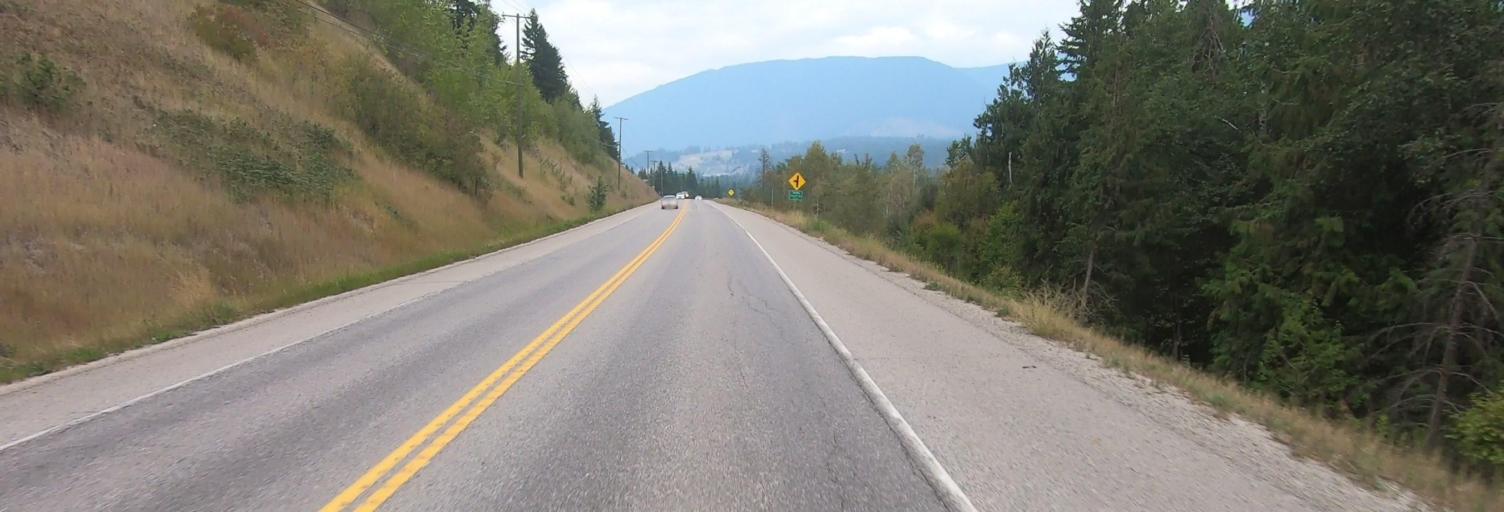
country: CA
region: British Columbia
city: Salmon Arm
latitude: 50.7815
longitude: -119.3370
